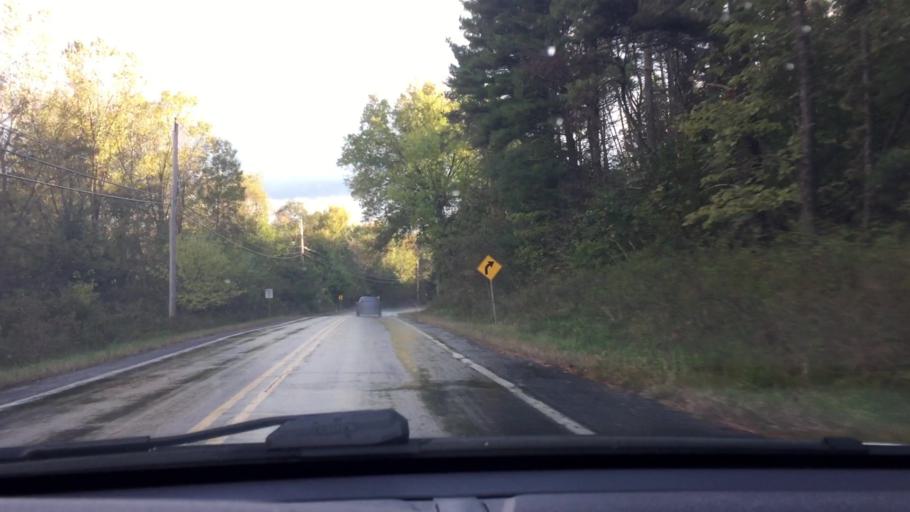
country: US
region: Pennsylvania
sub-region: Lawrence County
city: Oakwood
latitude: 41.0409
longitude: -80.4398
